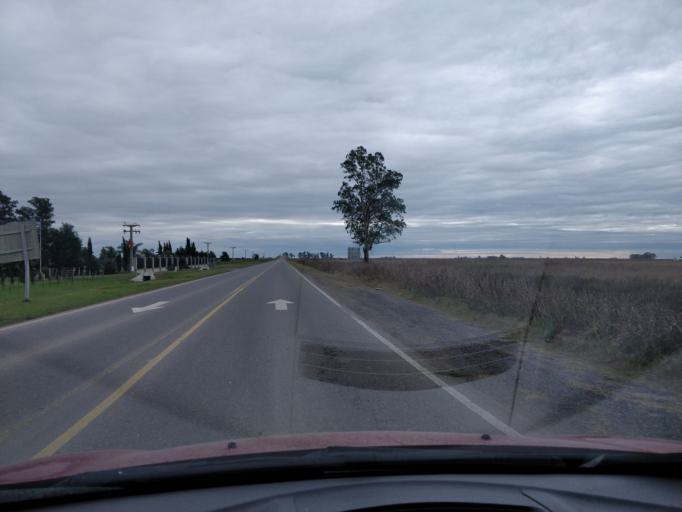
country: AR
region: Cordoba
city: Leones
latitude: -32.6414
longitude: -62.2901
